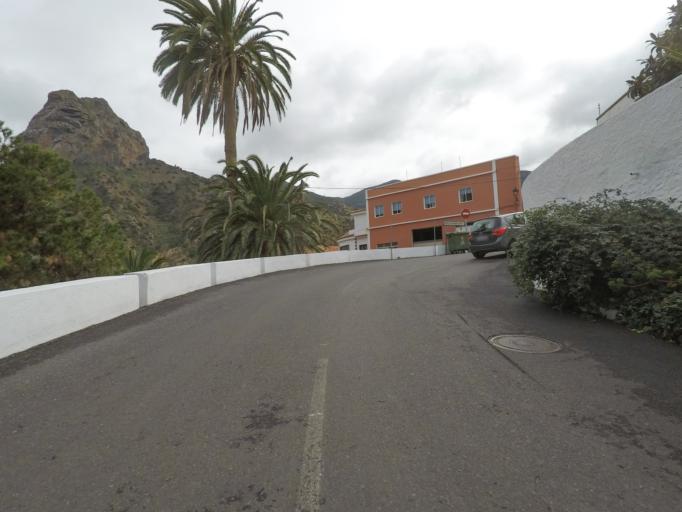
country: ES
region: Canary Islands
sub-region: Provincia de Santa Cruz de Tenerife
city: Vallehermosa
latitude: 28.1817
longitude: -17.2664
